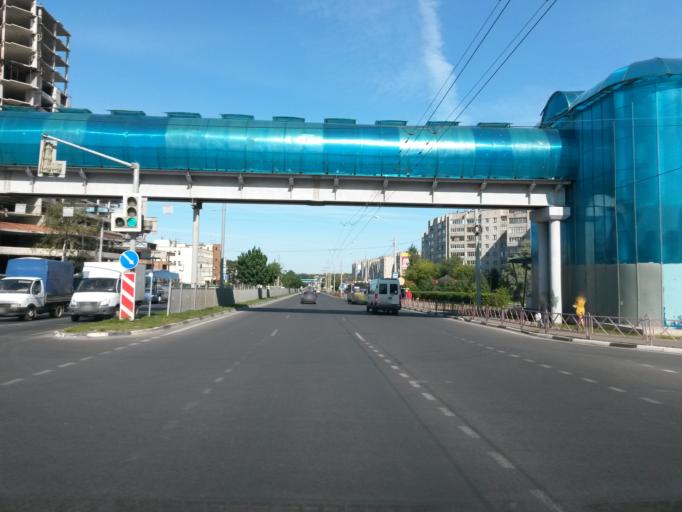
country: RU
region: Jaroslavl
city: Yaroslavl
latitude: 57.5928
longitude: 39.8637
